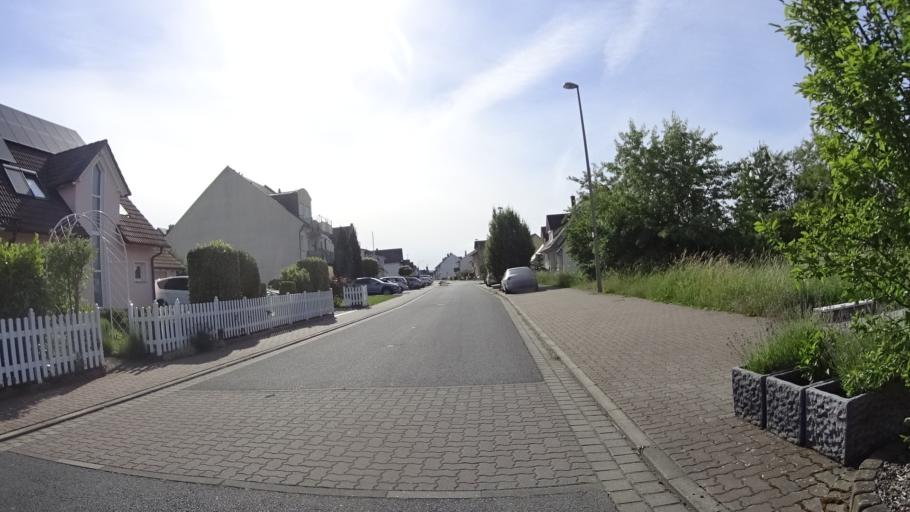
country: DE
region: Bavaria
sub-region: Regierungsbezirk Unterfranken
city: Stockstadt am Main
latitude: 49.9791
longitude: 9.0773
